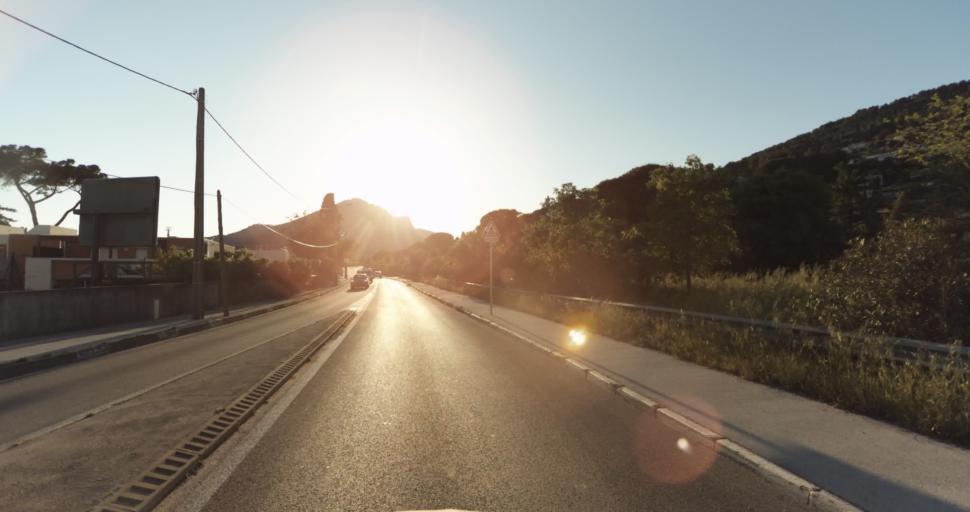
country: FR
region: Provence-Alpes-Cote d'Azur
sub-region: Departement du Var
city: La Valette-du-Var
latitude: 43.1422
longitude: 5.9995
